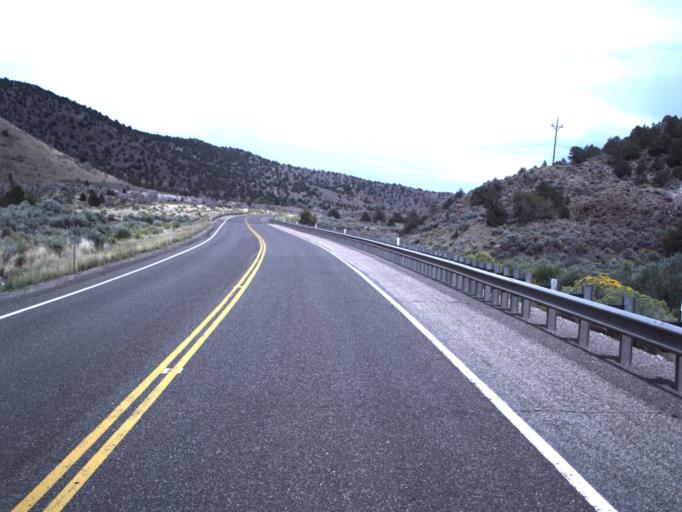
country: US
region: Utah
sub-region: Piute County
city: Junction
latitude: 38.1218
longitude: -112.3335
